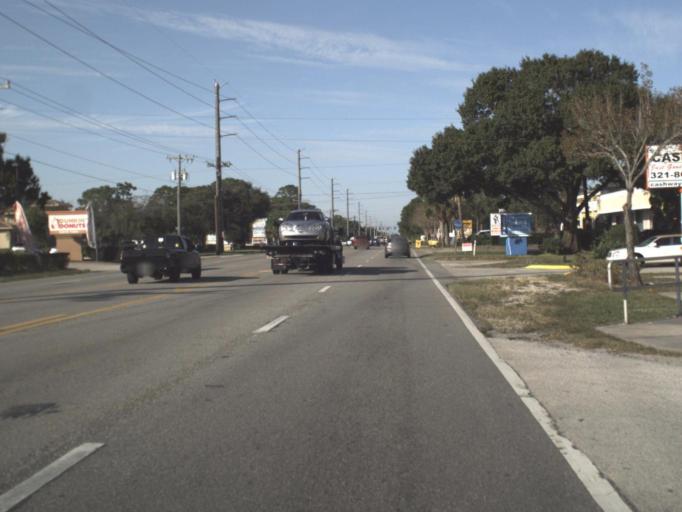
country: US
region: Florida
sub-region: Brevard County
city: June Park
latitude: 28.1015
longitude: -80.6725
